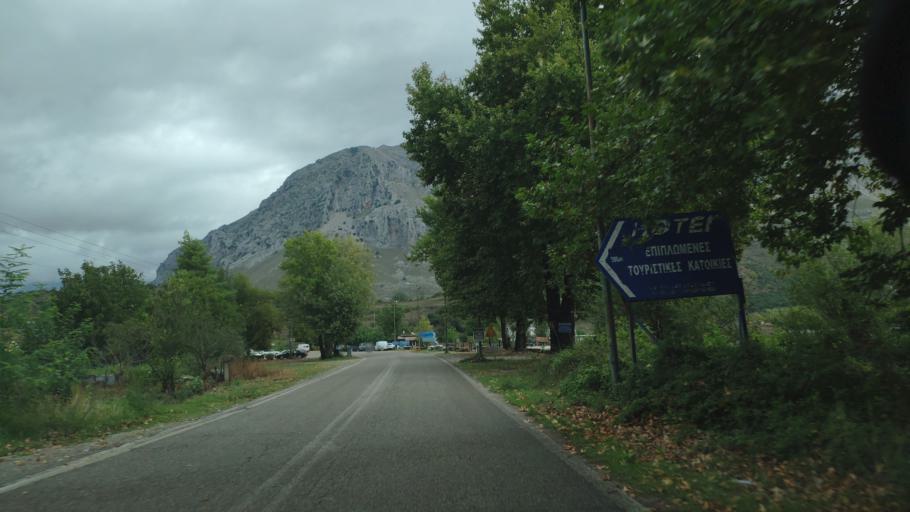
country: GR
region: West Greece
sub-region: Nomos Aitolias kai Akarnanias
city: Krikellos
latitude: 38.9716
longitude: 21.3306
